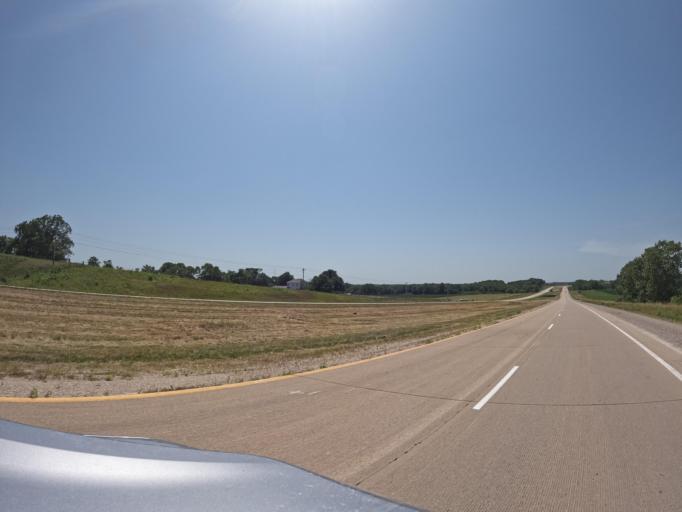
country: US
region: Iowa
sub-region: Henry County
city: Mount Pleasant
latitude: 40.9761
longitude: -91.6687
